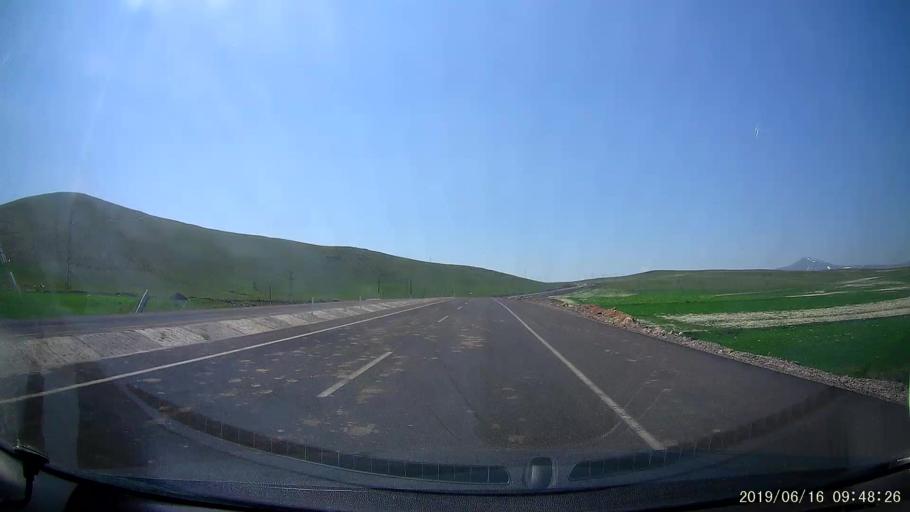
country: TR
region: Kars
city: Digor
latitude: 40.4340
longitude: 43.3530
